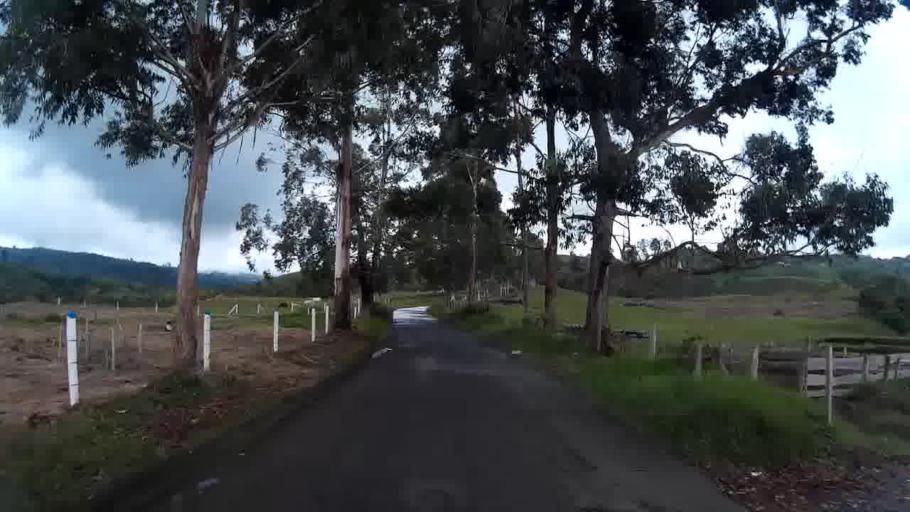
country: CO
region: Quindio
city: Filandia
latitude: 4.6860
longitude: -75.6600
